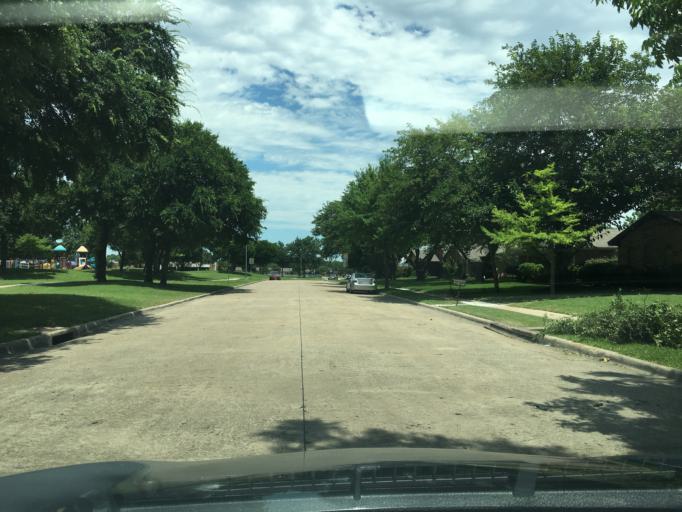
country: US
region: Texas
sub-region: Dallas County
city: Richardson
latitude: 32.9368
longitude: -96.6893
